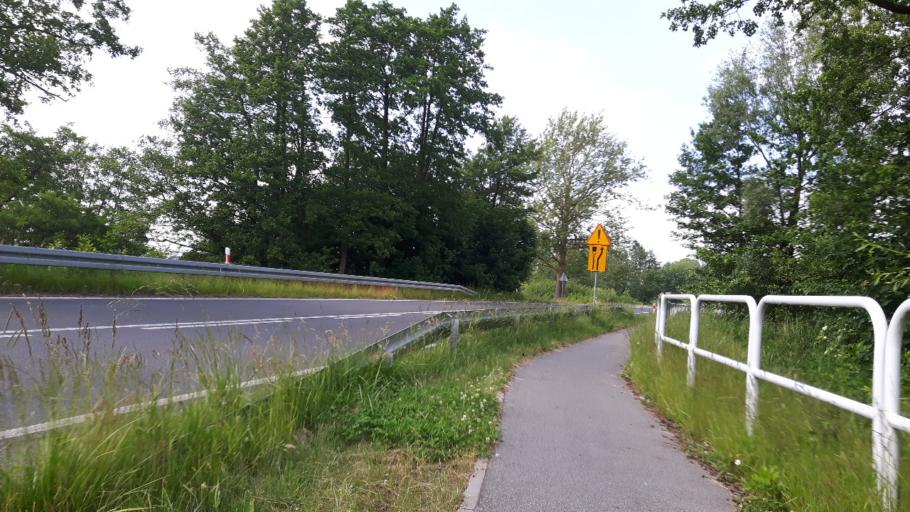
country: PL
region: West Pomeranian Voivodeship
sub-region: Powiat slawienski
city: Darlowo
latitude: 54.3500
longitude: 16.3328
